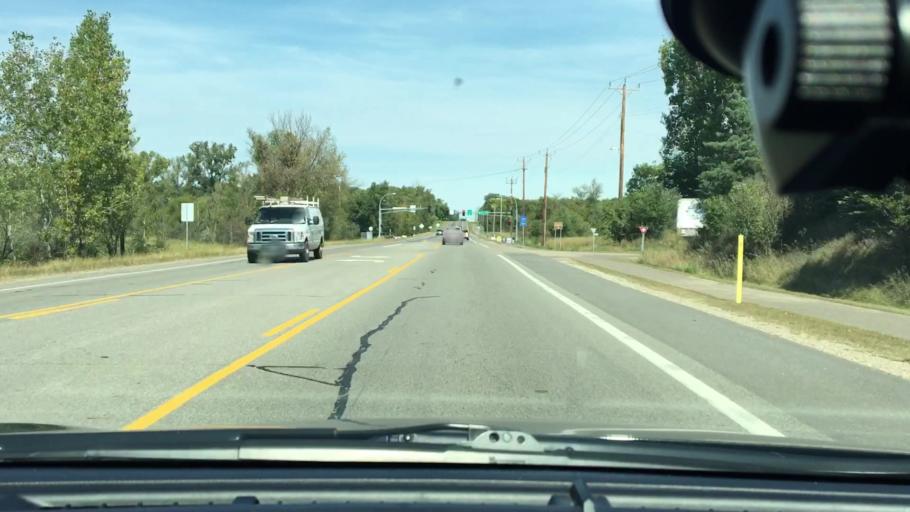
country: US
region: Minnesota
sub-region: Wright County
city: Hanover
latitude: 45.1601
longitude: -93.6660
